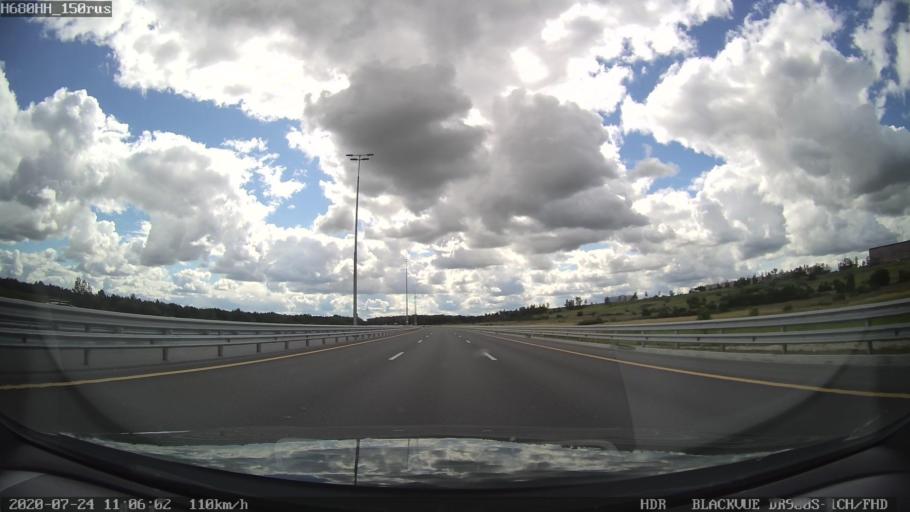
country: RU
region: St.-Petersburg
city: Shushary
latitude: 59.7689
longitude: 30.3660
